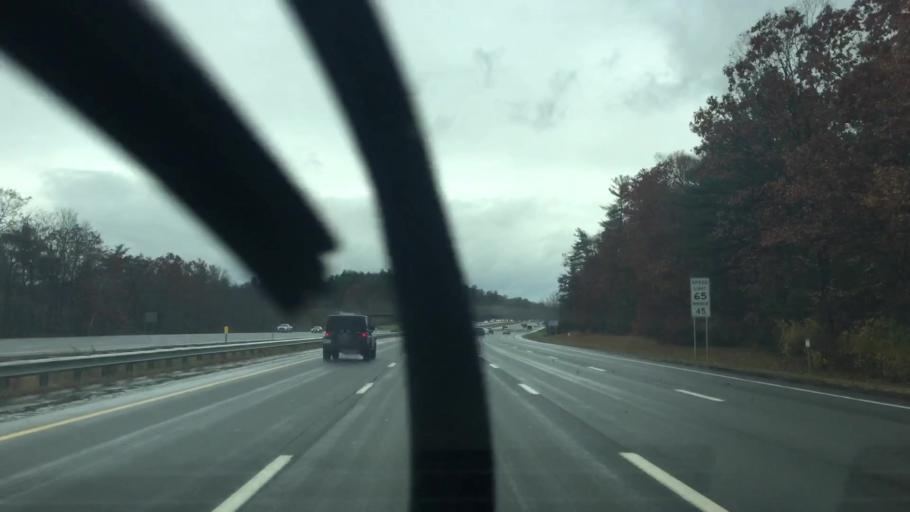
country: US
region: New Hampshire
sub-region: Rockingham County
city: Seabrook
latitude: 42.9039
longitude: -70.8776
